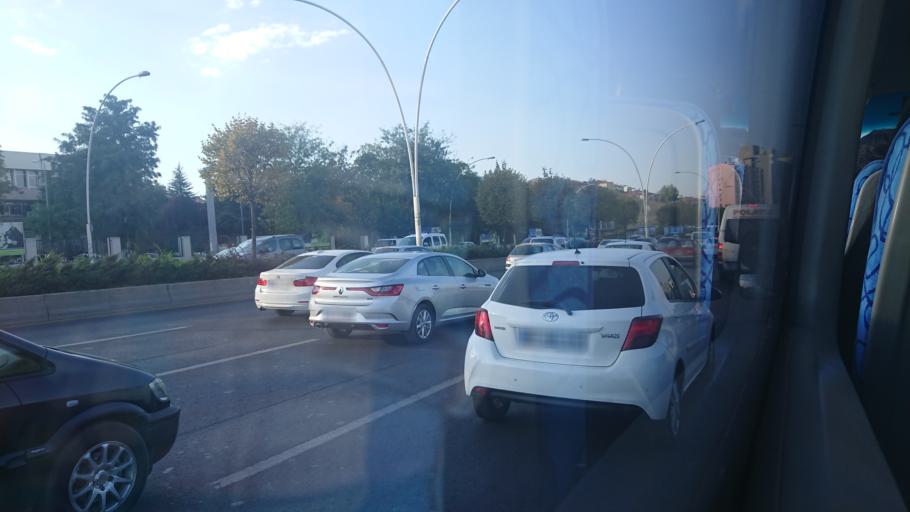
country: TR
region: Ankara
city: Ankara
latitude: 39.9208
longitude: 32.8144
